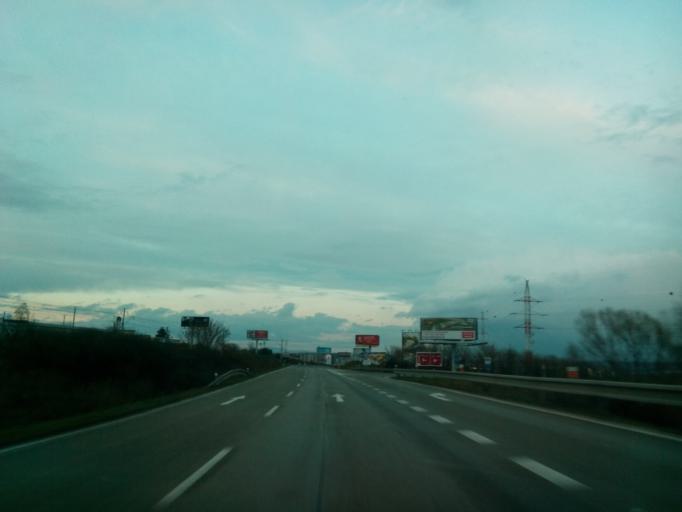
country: SK
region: Kosicky
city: Kosice
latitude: 48.6870
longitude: 21.2230
